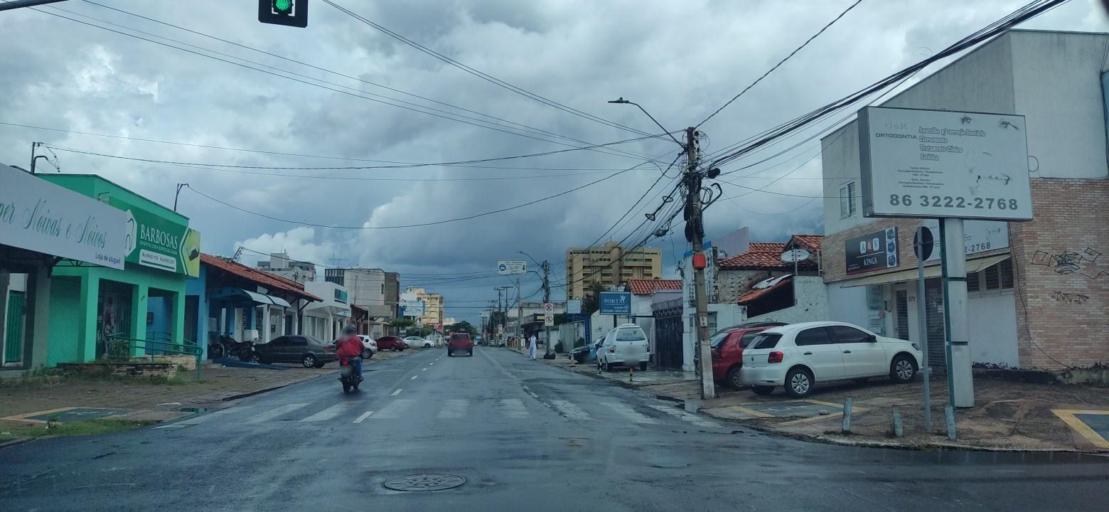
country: BR
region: Piaui
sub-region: Teresina
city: Teresina
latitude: -5.0833
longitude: -42.8088
